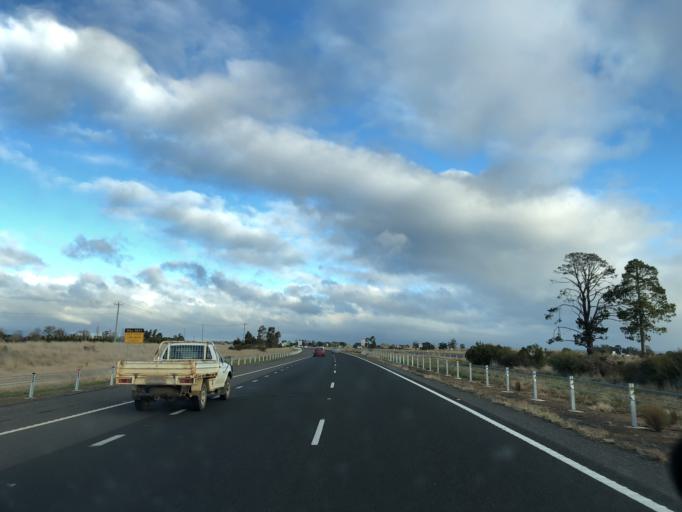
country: AU
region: Victoria
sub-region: Mount Alexander
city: Castlemaine
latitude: -37.1968
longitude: 144.4054
